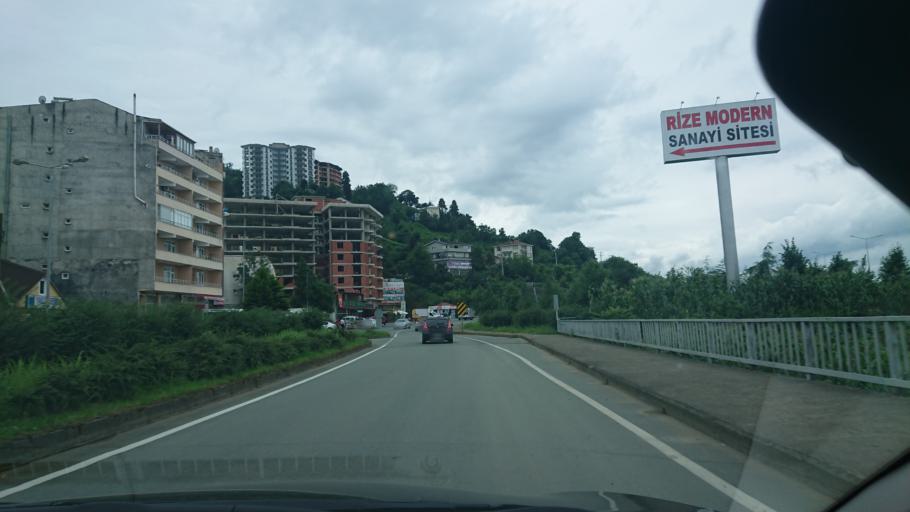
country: TR
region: Rize
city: Rize
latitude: 41.0347
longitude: 40.4792
